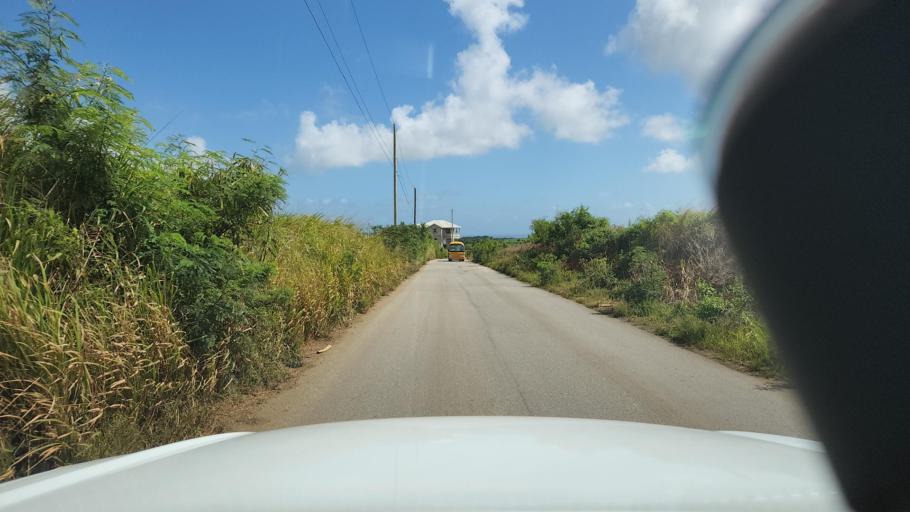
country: BB
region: Saint John
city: Four Cross Roads
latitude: 13.1746
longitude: -59.4919
